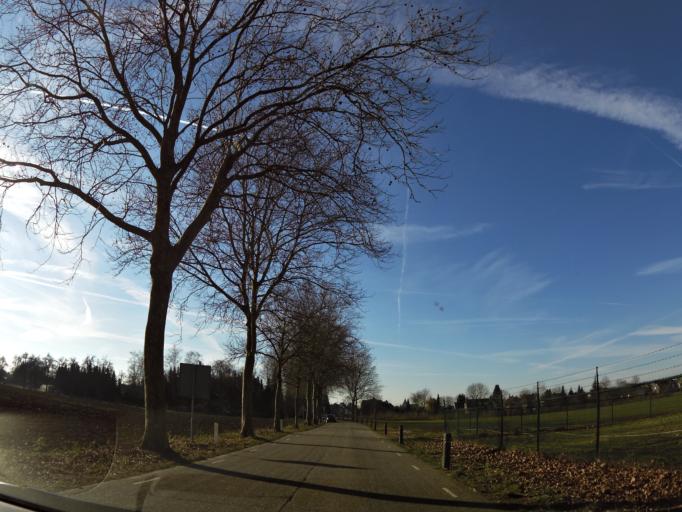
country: NL
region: Limburg
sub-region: Gemeente Sittard-Geleen
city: Sittard
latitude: 51.0407
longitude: 5.8706
